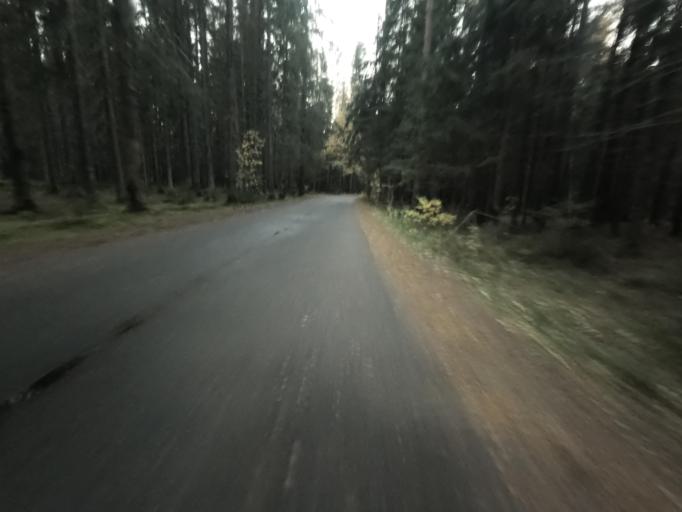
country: RU
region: St.-Petersburg
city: Komarovo
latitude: 60.2072
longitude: 29.7970
